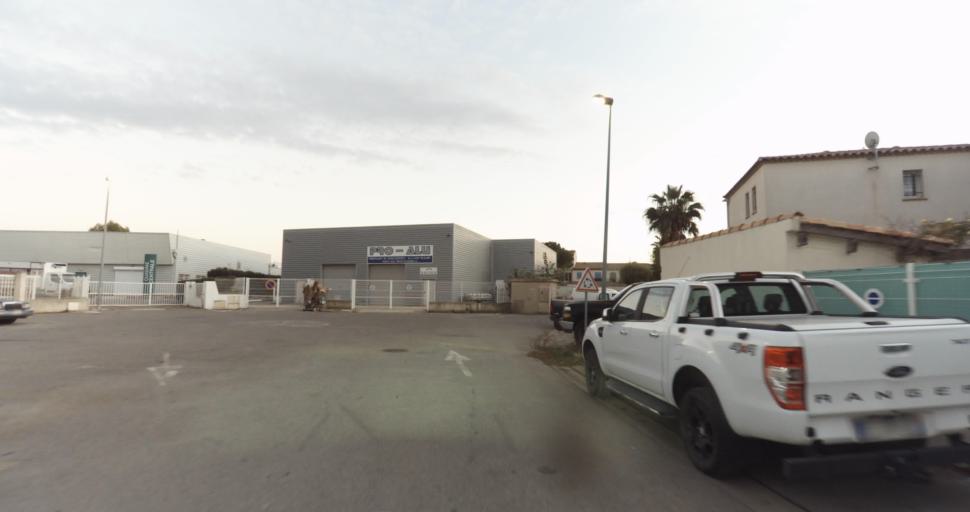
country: FR
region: Languedoc-Roussillon
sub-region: Departement du Gard
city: Aigues-Mortes
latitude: 43.5765
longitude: 4.1860
